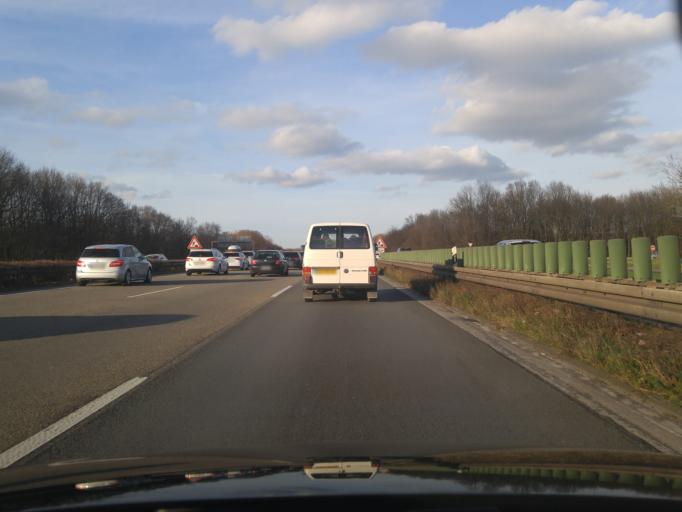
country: DE
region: North Rhine-Westphalia
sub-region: Regierungsbezirk Dusseldorf
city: Hilden
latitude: 51.1923
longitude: 6.9409
